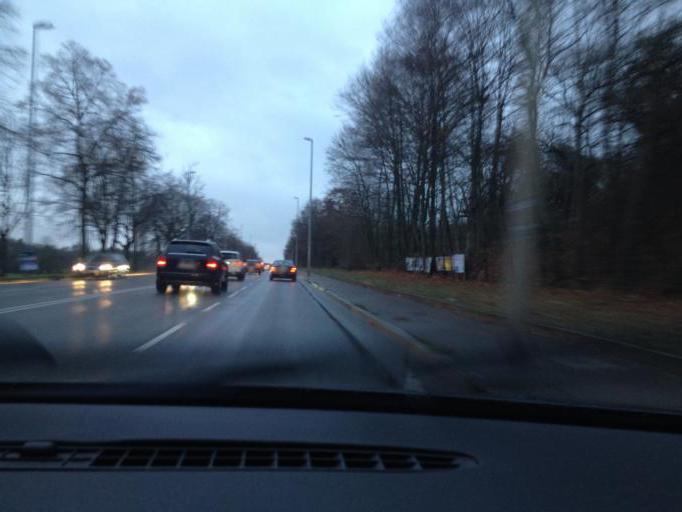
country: DE
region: Baden-Wuerttemberg
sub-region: Regierungsbezirk Stuttgart
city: Ludwigsburg
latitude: 48.9032
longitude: 9.1837
